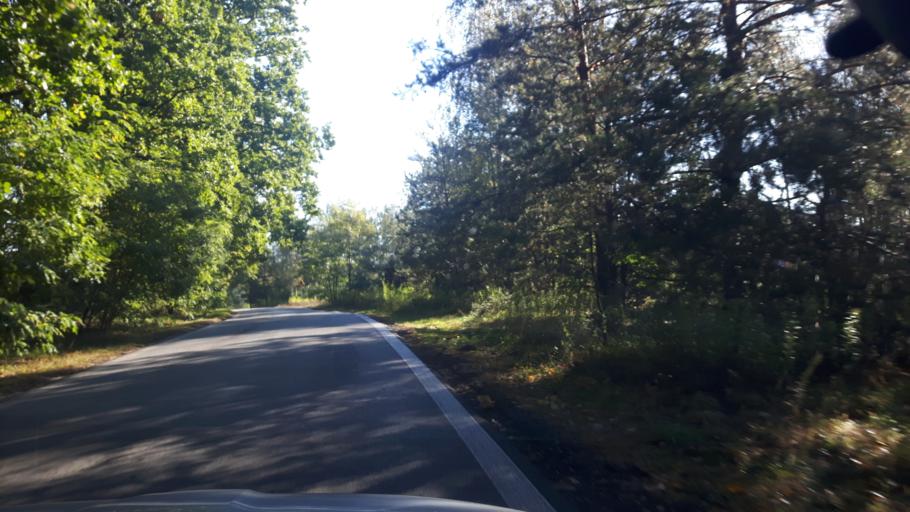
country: PL
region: Masovian Voivodeship
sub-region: Warszawa
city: Bialoleka
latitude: 52.3495
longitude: 21.0107
